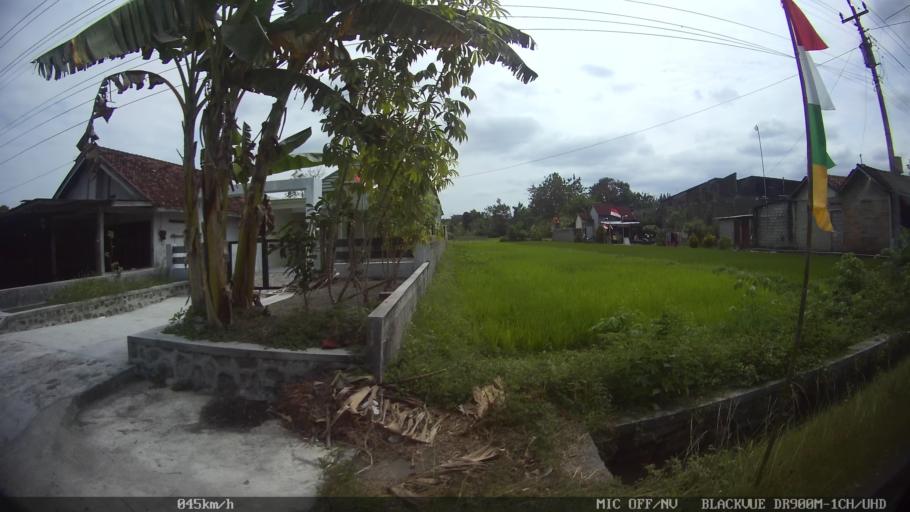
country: ID
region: Central Java
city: Candi Prambanan
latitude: -7.7461
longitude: 110.4811
